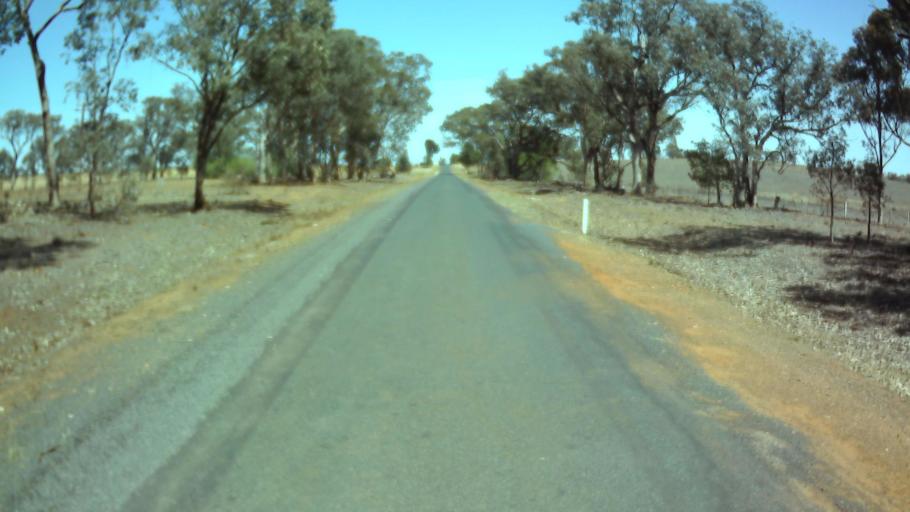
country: AU
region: New South Wales
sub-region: Weddin
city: Grenfell
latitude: -33.8645
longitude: 147.9991
